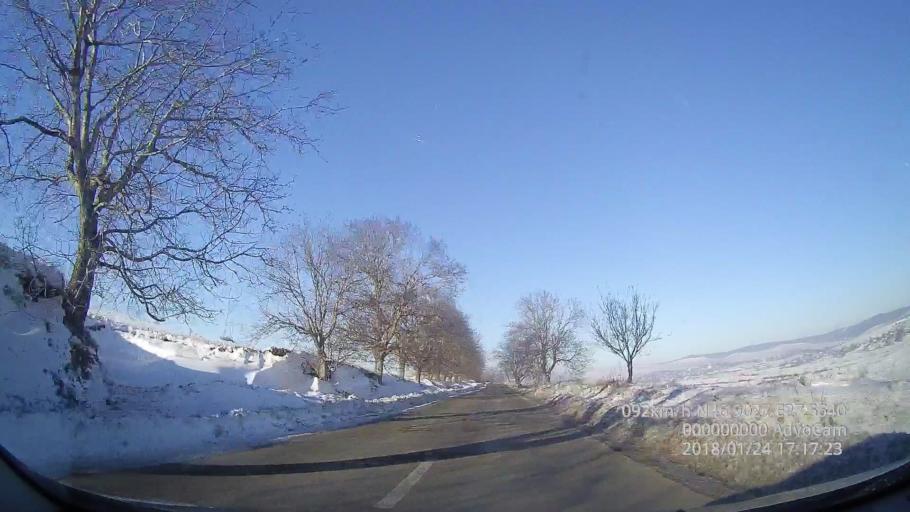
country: RO
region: Iasi
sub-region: Comuna Scanteia
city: Scanteia
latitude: 46.9034
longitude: 27.5641
